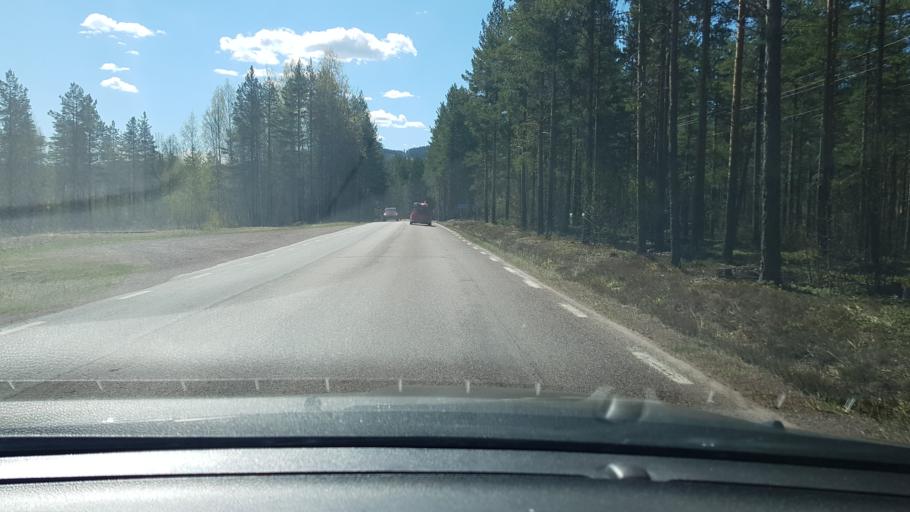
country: SE
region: Dalarna
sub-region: Alvdalens Kommun
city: AElvdalen
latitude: 61.1255
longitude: 14.1732
